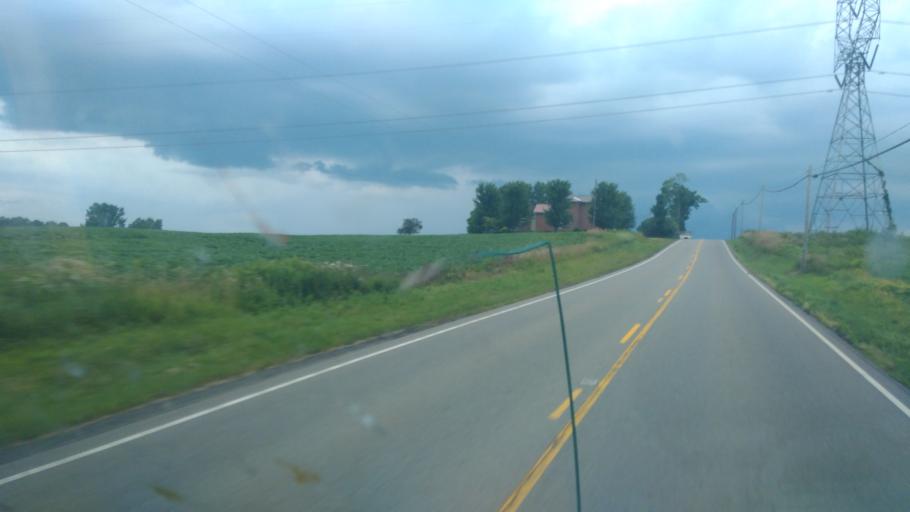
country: US
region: Ohio
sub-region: Licking County
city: Granville
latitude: 40.0983
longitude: -82.5196
